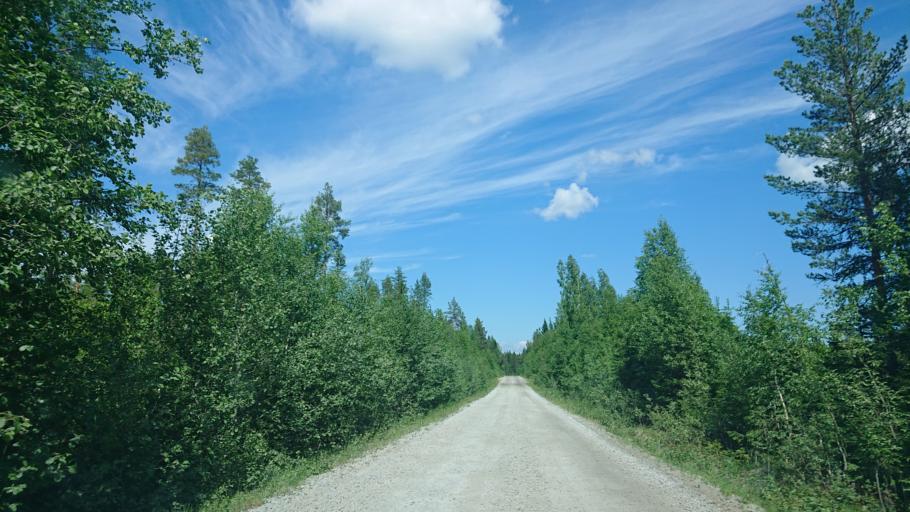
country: SE
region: Vaesternorrland
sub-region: Solleftea Kommun
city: Solleftea
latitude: 62.9545
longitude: 17.1431
